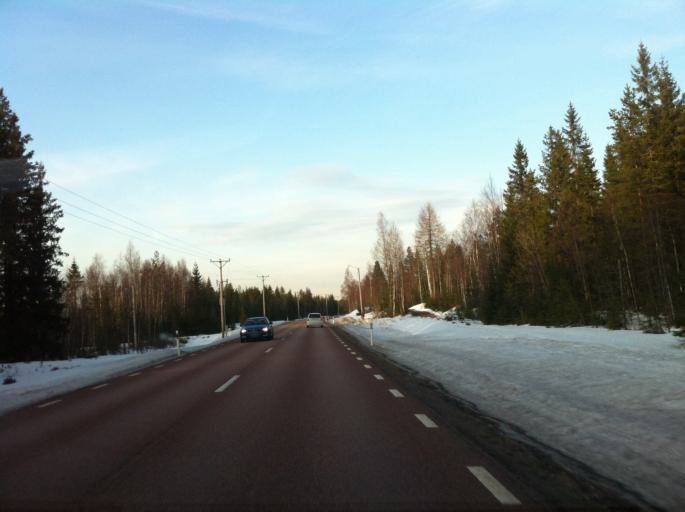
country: SE
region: Dalarna
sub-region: Vansbro Kommun
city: Vansbro
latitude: 60.2776
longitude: 14.1701
